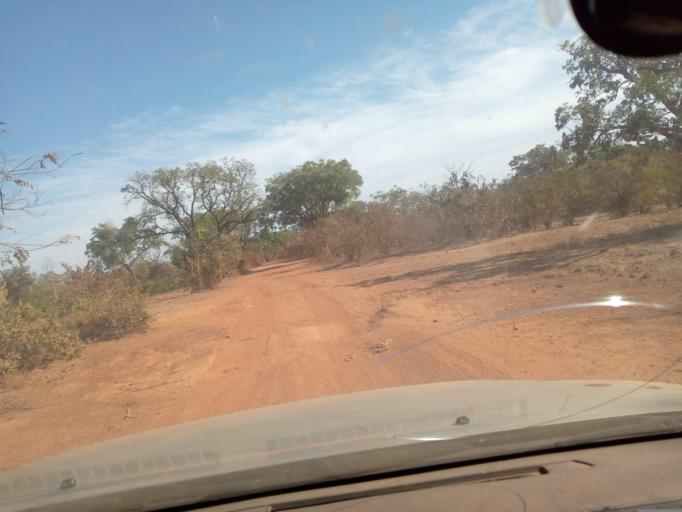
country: ML
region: Sikasso
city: Sikasso
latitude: 11.4705
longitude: -5.3291
